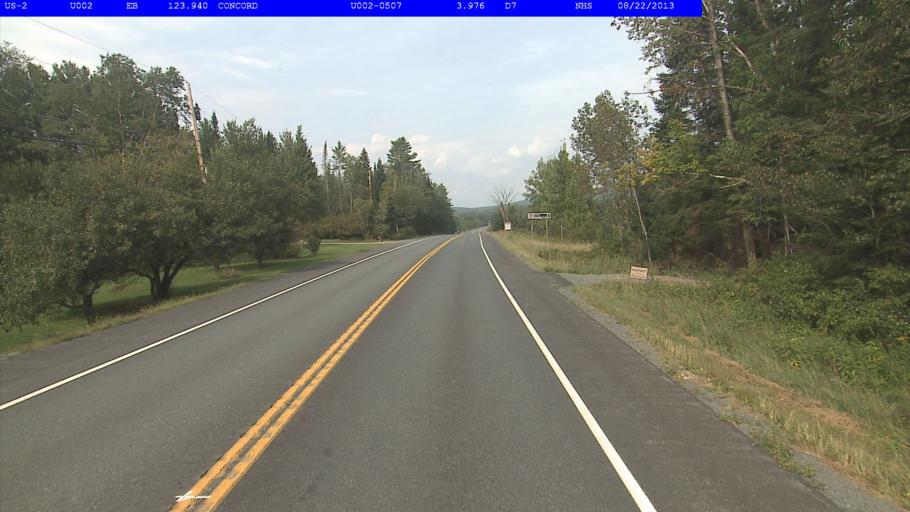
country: US
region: Vermont
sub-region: Caledonia County
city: St Johnsbury
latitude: 44.4506
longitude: -71.8724
